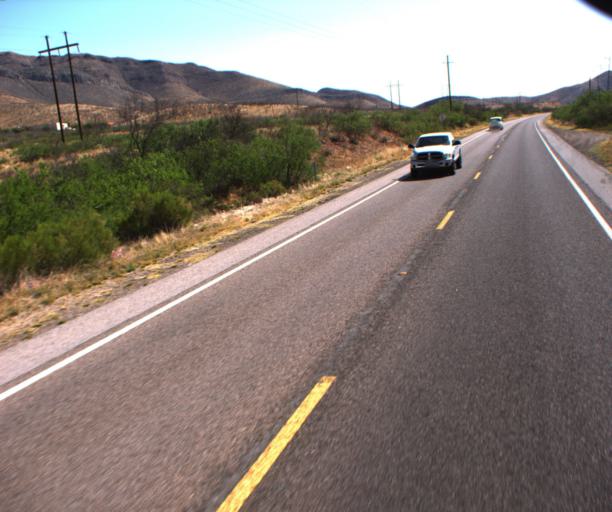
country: US
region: Arizona
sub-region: Cochise County
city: Bisbee
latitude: 31.4292
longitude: -109.8749
